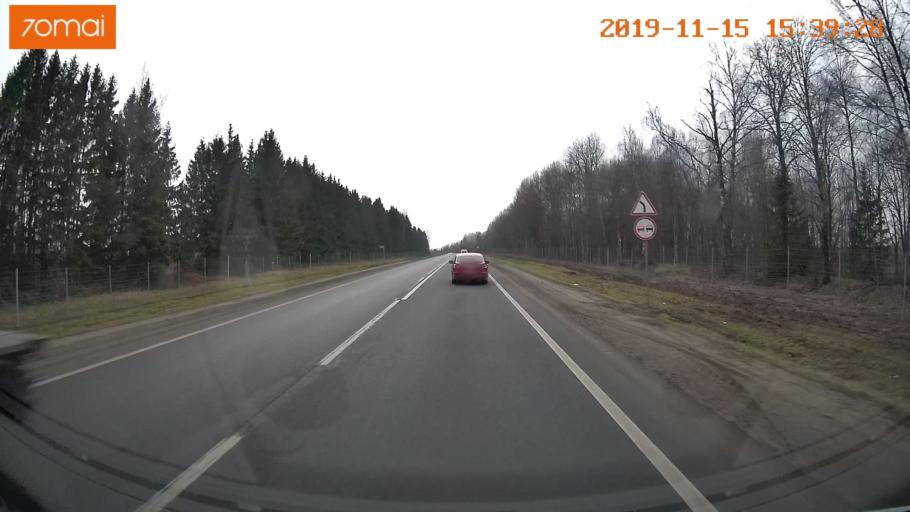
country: RU
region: Jaroslavl
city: Danilov
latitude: 58.0207
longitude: 40.0677
